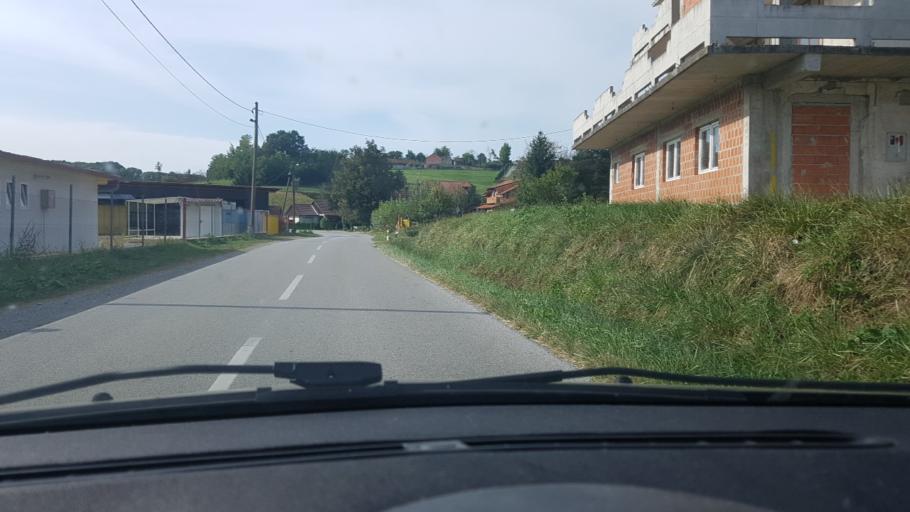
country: HR
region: Krapinsko-Zagorska
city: Mihovljan
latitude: 46.1281
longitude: 15.9764
